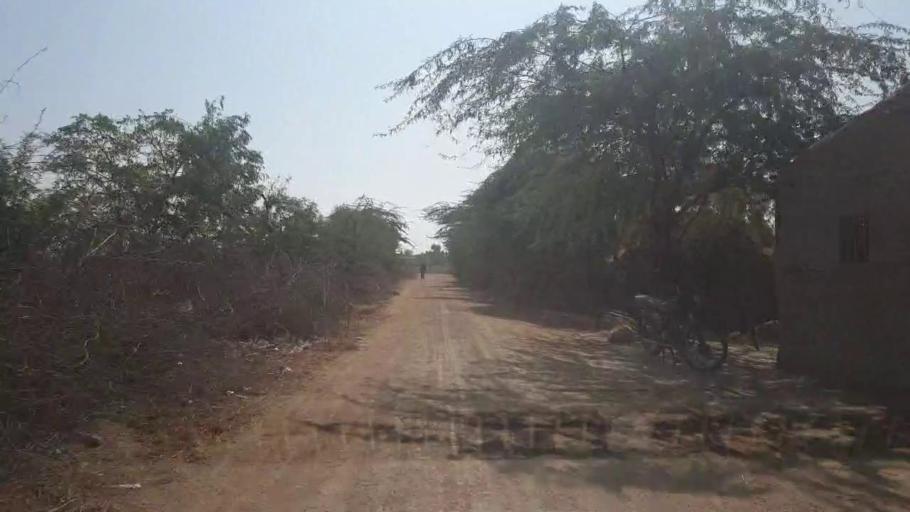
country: PK
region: Sindh
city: Badin
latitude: 24.5489
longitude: 68.8450
